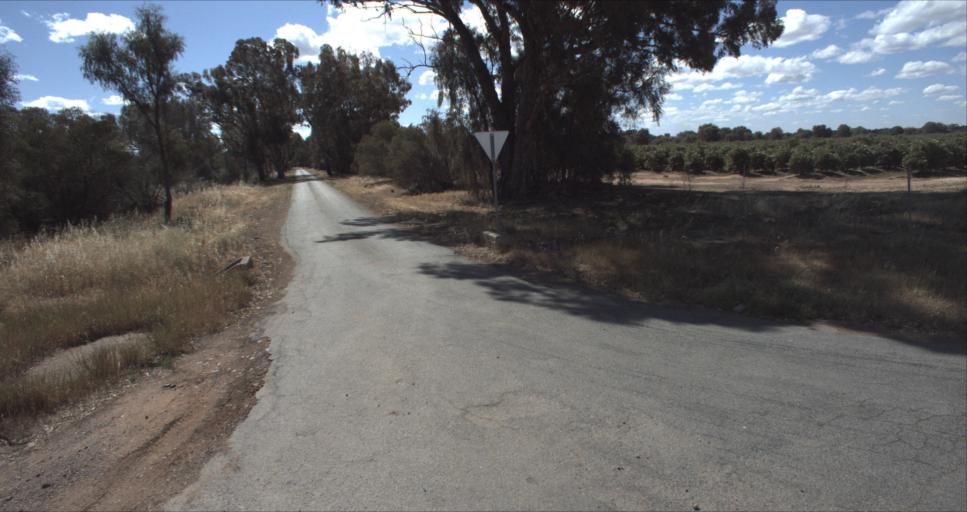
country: AU
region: New South Wales
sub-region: Leeton
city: Leeton
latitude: -34.5168
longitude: 146.2363
